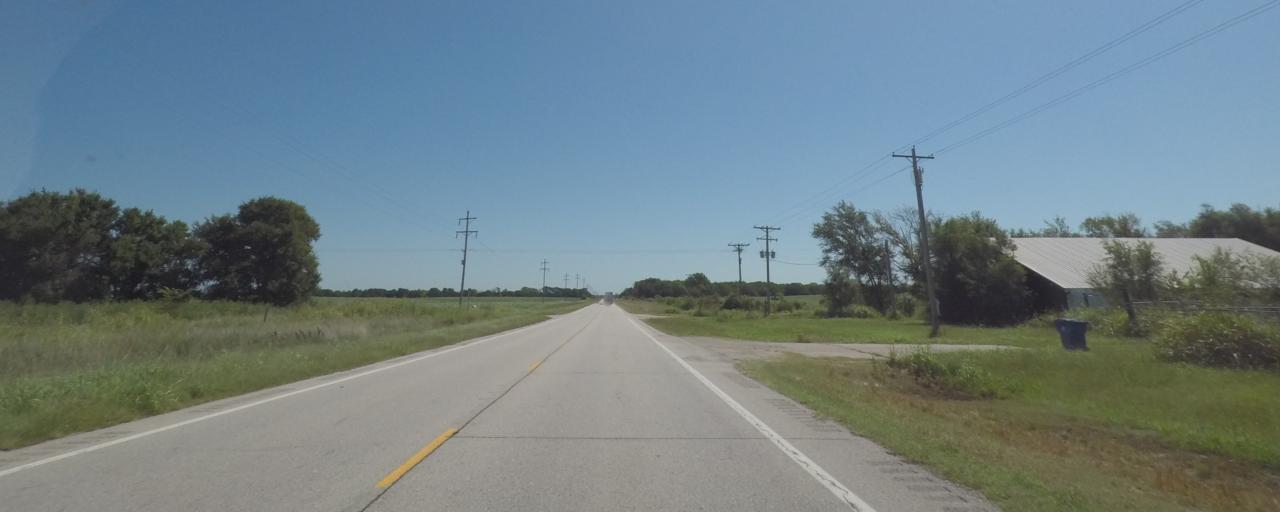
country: US
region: Kansas
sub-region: Sumner County
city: Belle Plaine
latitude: 37.3913
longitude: -97.3680
